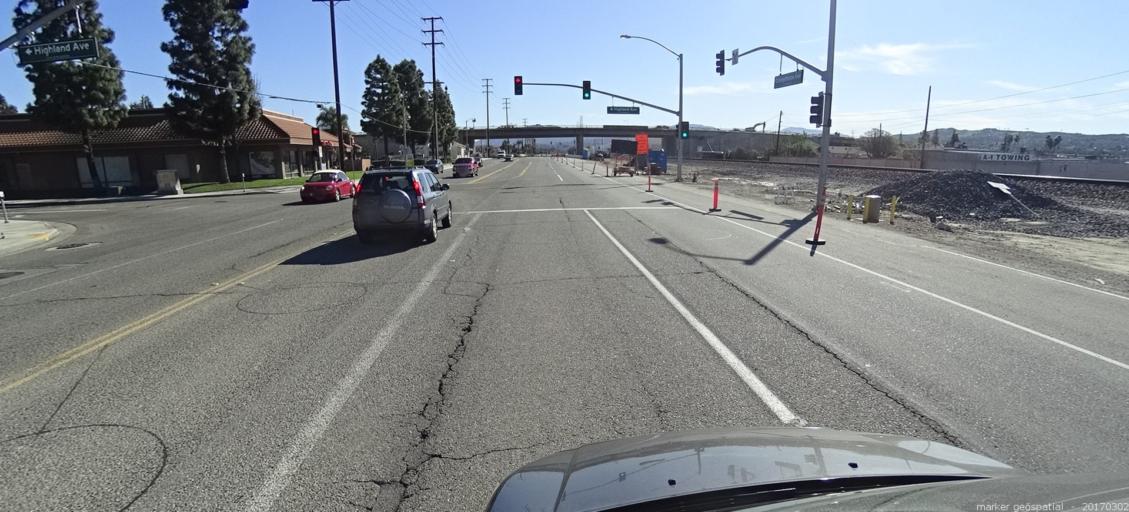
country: US
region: California
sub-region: Orange County
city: Yorba Linda
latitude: 33.8670
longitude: -117.8208
